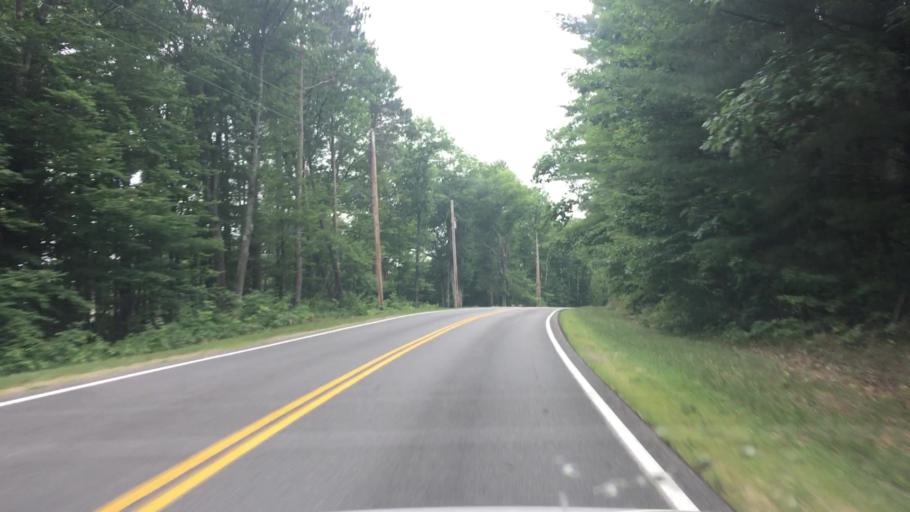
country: US
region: New York
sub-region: Clinton County
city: Morrisonville
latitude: 44.6154
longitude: -73.6257
